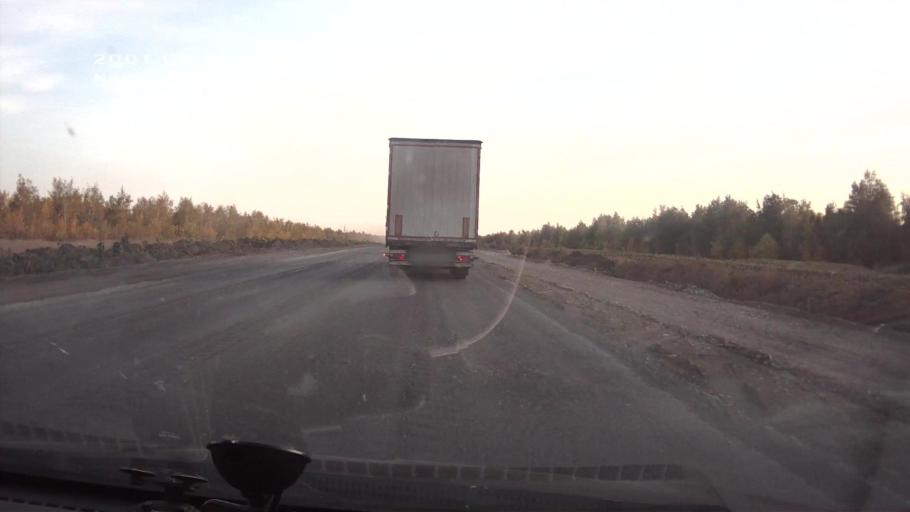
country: RU
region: Saratov
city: Kamenskiy
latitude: 50.9308
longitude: 45.6000
